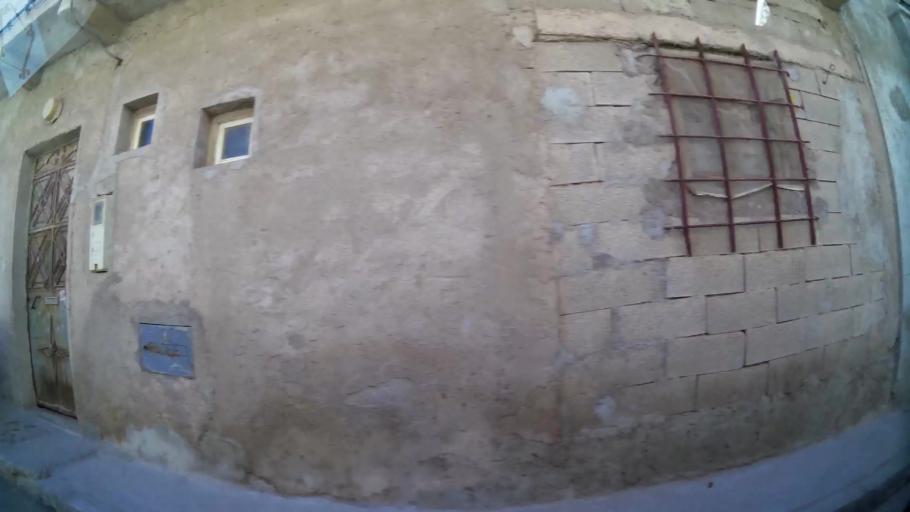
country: MA
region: Oriental
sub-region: Oujda-Angad
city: Oujda
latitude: 34.6460
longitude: -1.9478
